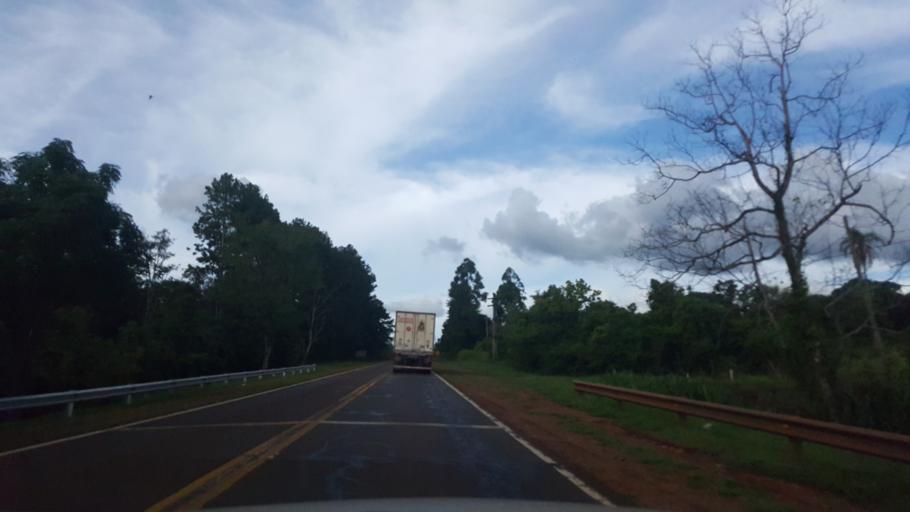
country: AR
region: Misiones
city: Gobernador Roca
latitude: -27.2005
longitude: -55.4801
